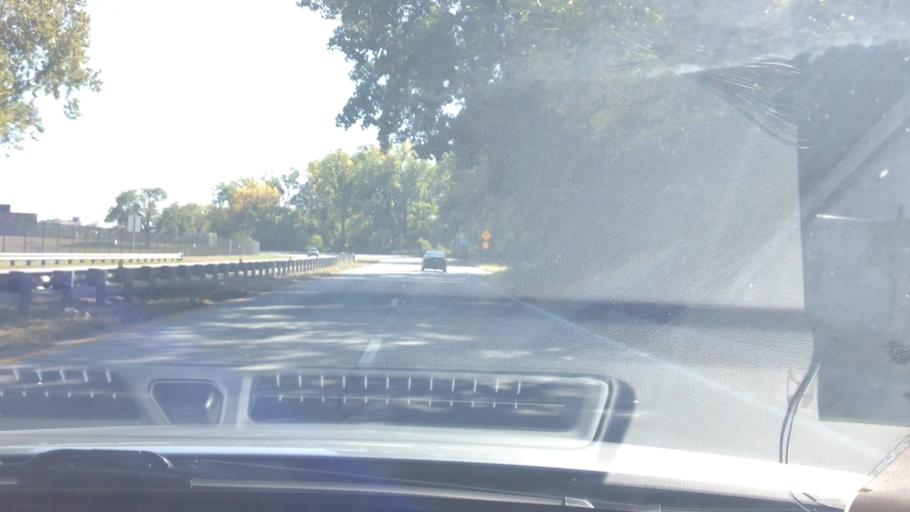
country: US
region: Missouri
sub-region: Platte County
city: Riverside
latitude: 39.1555
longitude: -94.5860
